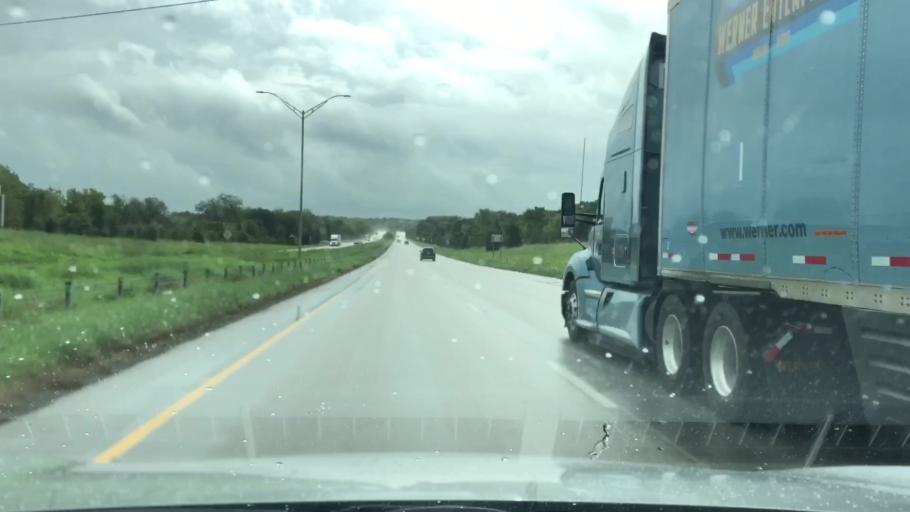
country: US
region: Texas
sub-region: Fayette County
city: Schulenburg
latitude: 29.6928
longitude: -96.8454
